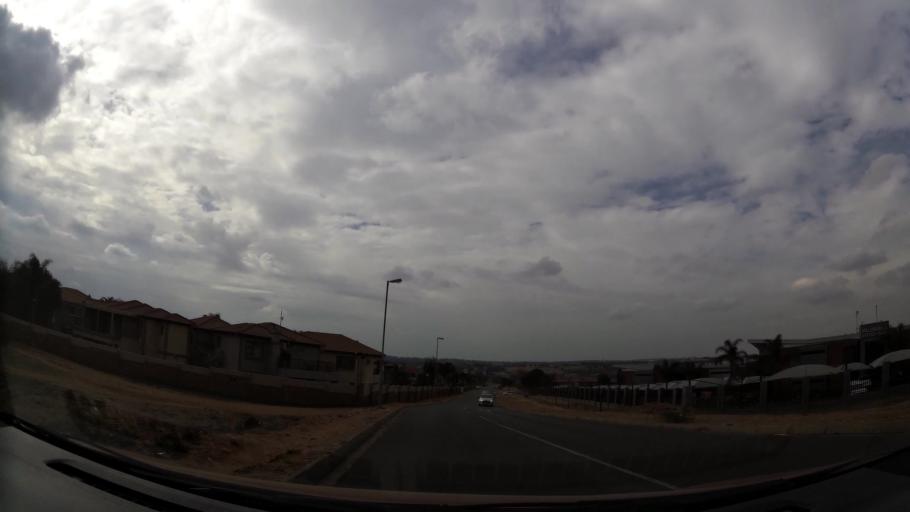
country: ZA
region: Gauteng
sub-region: City of Johannesburg Metropolitan Municipality
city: Roodepoort
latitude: -26.0979
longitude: 27.8753
